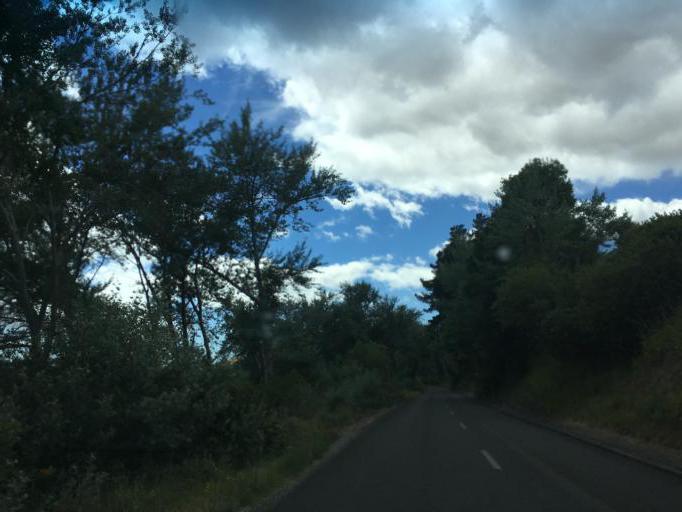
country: NZ
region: Hawke's Bay
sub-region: Hastings District
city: Hastings
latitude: -39.7346
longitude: 176.9028
